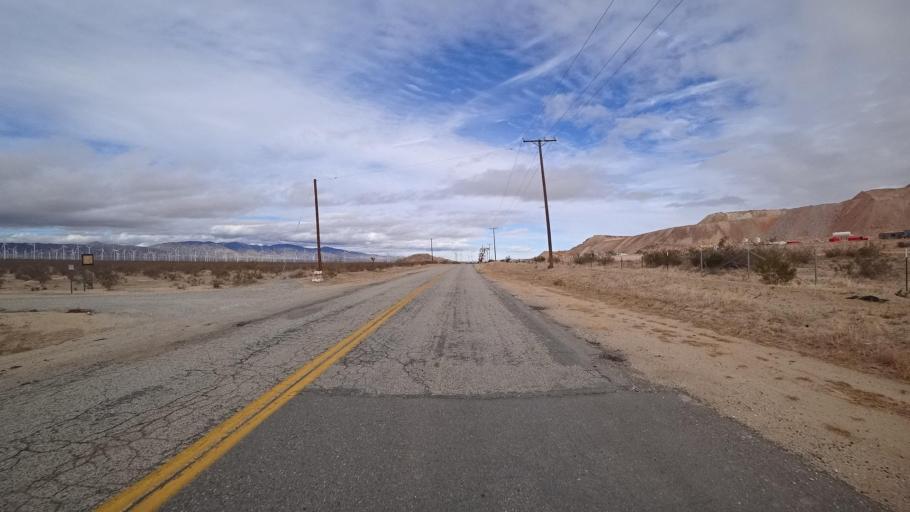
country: US
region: California
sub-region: Kern County
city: Mojave
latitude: 34.9869
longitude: -118.2079
